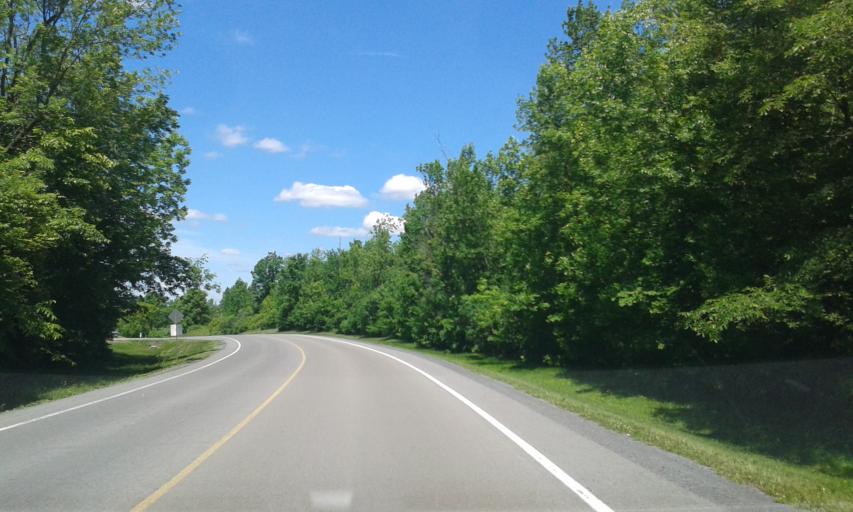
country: US
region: New York
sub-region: St. Lawrence County
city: Massena
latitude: 45.0185
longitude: -74.8930
